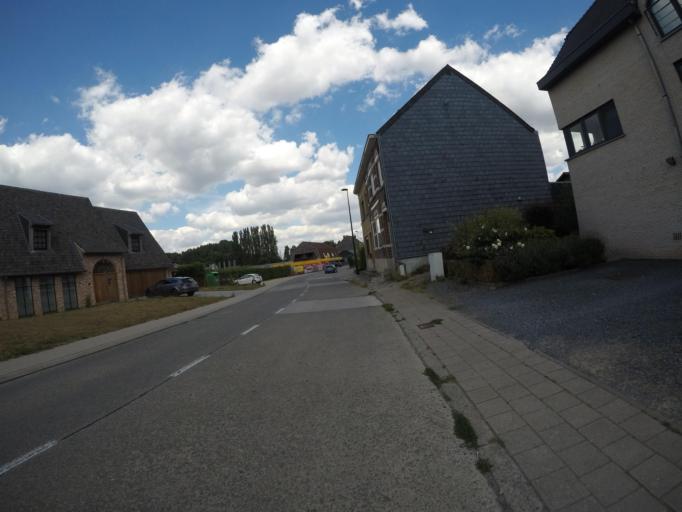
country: BE
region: Flanders
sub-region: Provincie Vlaams-Brabant
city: Ternat
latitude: 50.8456
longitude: 4.1332
